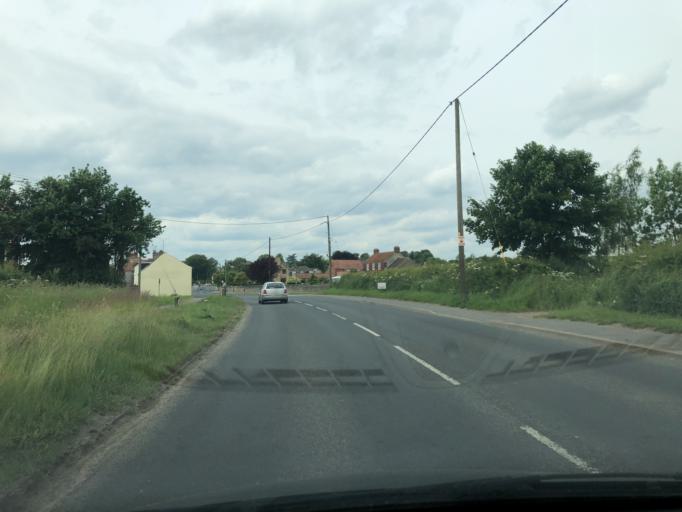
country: GB
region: England
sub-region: North Yorkshire
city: Pickering
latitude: 54.2553
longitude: -0.7960
